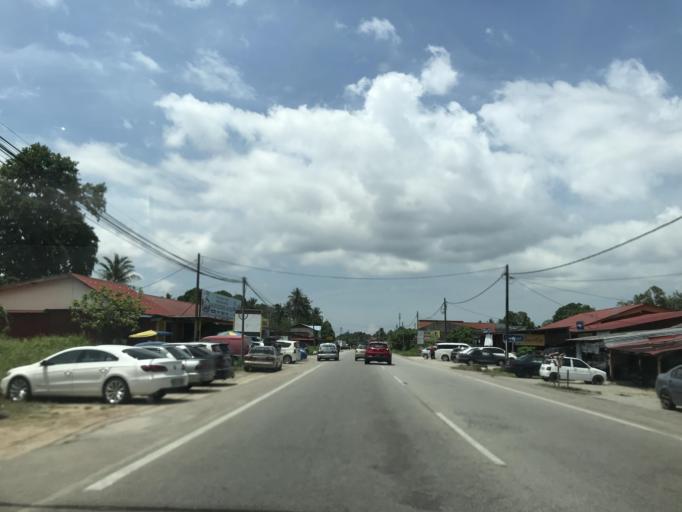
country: MY
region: Kelantan
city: Pasir Mas
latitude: 6.0580
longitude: 102.1995
